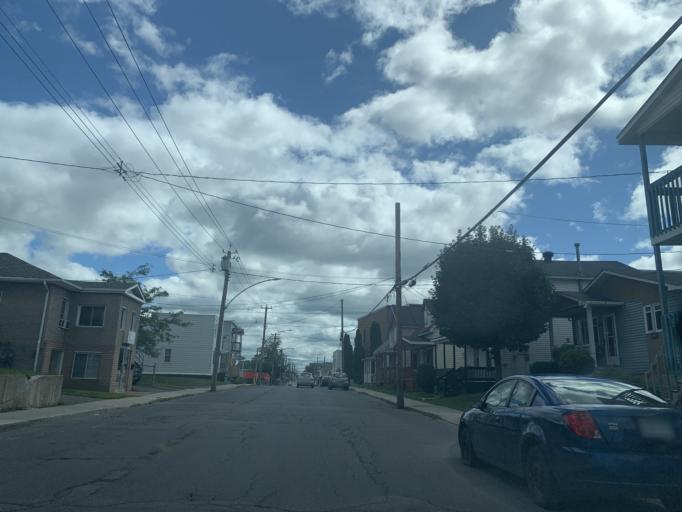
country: CA
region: Ontario
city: Hawkesbury
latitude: 45.6082
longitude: -74.6108
